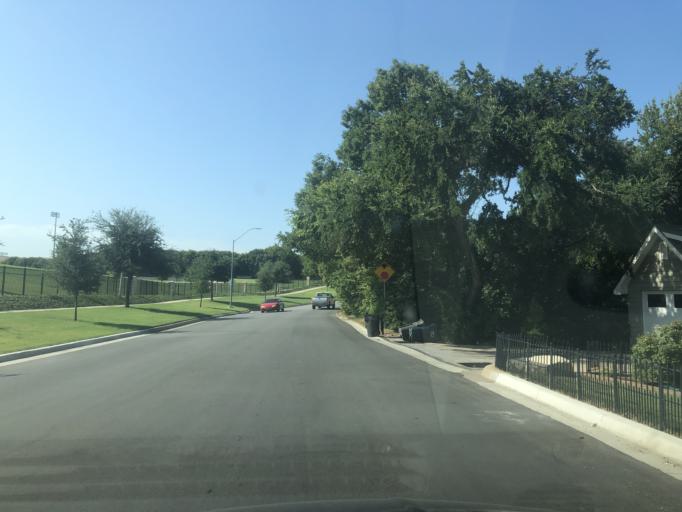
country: US
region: Texas
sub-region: Tarrant County
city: Fort Worth
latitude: 32.7056
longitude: -97.3742
